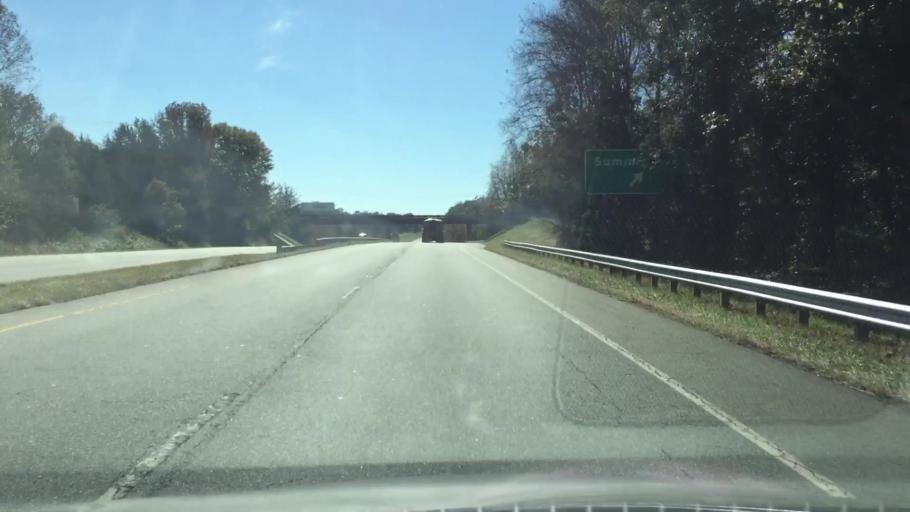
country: US
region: North Carolina
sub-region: Guilford County
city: McLeansville
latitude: 36.1776
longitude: -79.7108
